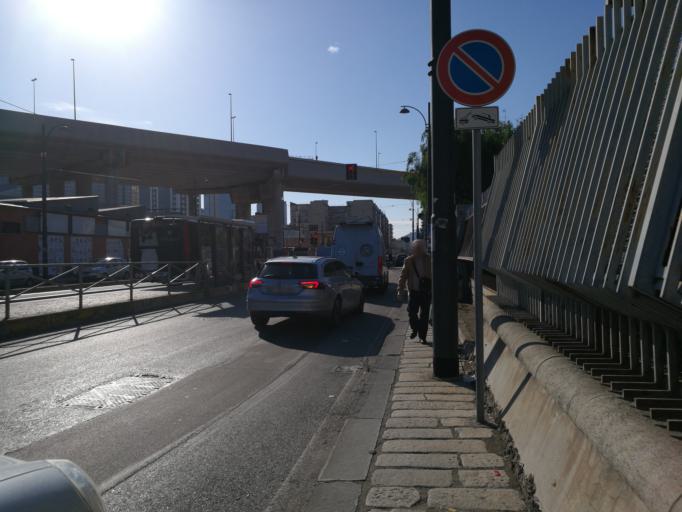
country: IT
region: Campania
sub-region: Provincia di Napoli
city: Casavatore
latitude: 40.8644
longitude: 14.2859
